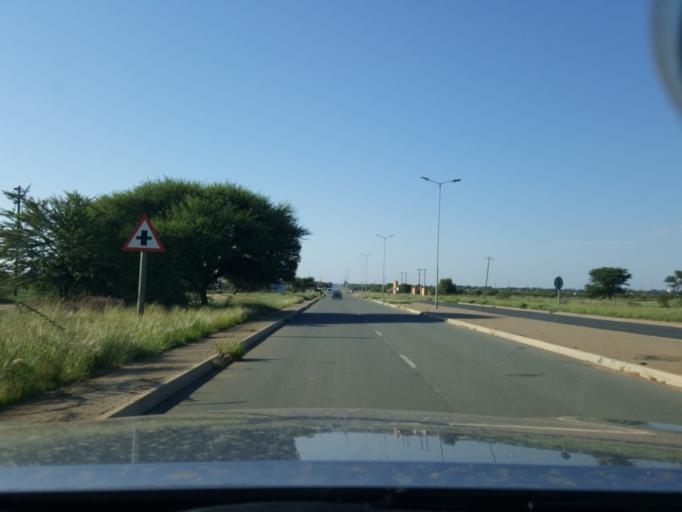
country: ZA
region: North-West
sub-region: Ngaka Modiri Molema District Municipality
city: Mmabatho
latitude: -25.7977
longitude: 25.6309
